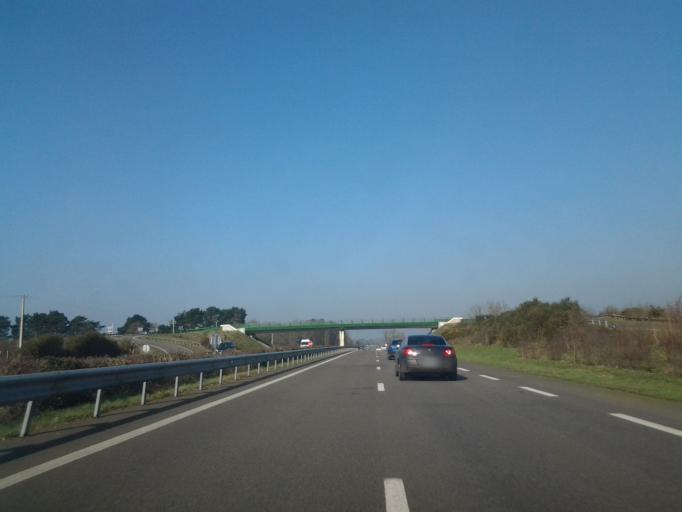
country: FR
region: Pays de la Loire
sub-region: Departement de la Vendee
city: Saint-Christophe-du-Ligneron
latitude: 46.8018
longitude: -1.7281
